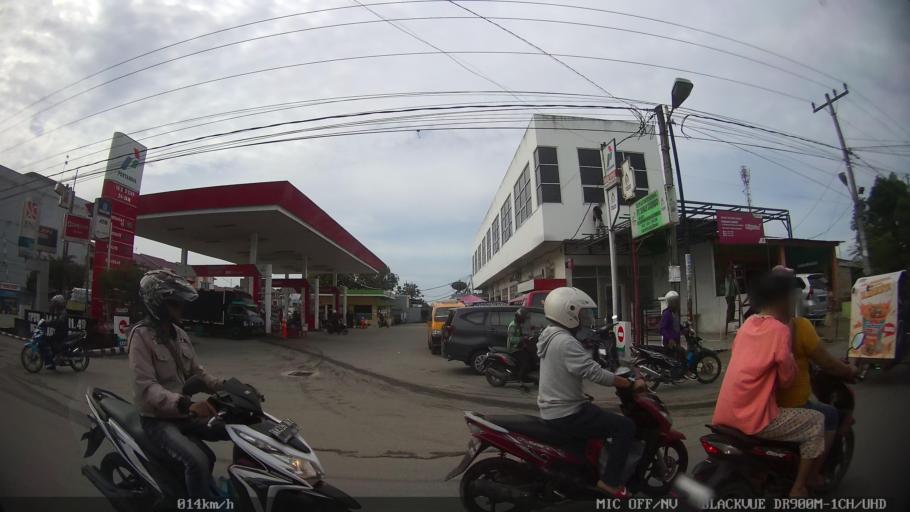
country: ID
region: North Sumatra
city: Medan
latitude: 3.6199
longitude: 98.7414
